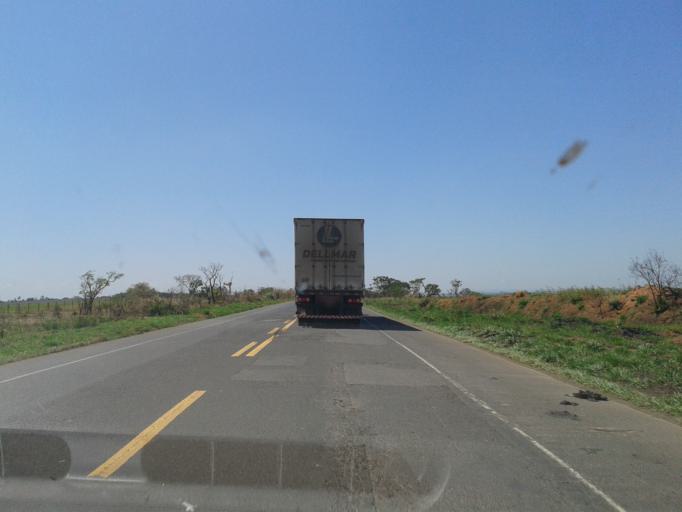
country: BR
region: Minas Gerais
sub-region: Araxa
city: Araxa
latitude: -19.4326
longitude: -47.2211
